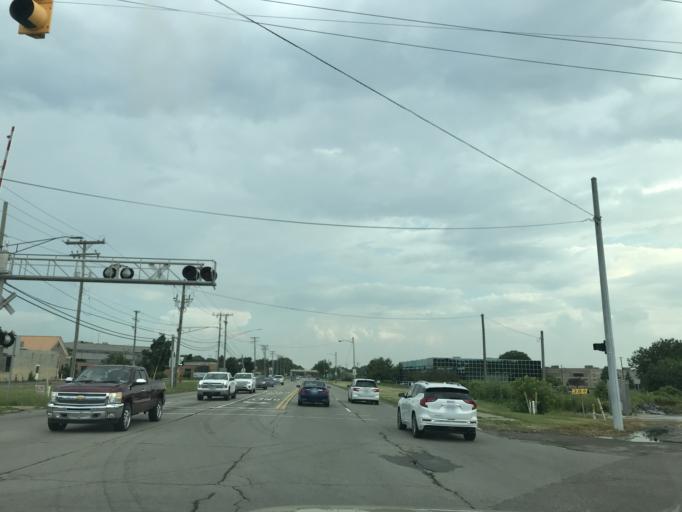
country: US
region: Michigan
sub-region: Wayne County
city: Southgate
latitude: 42.2131
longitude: -83.2292
